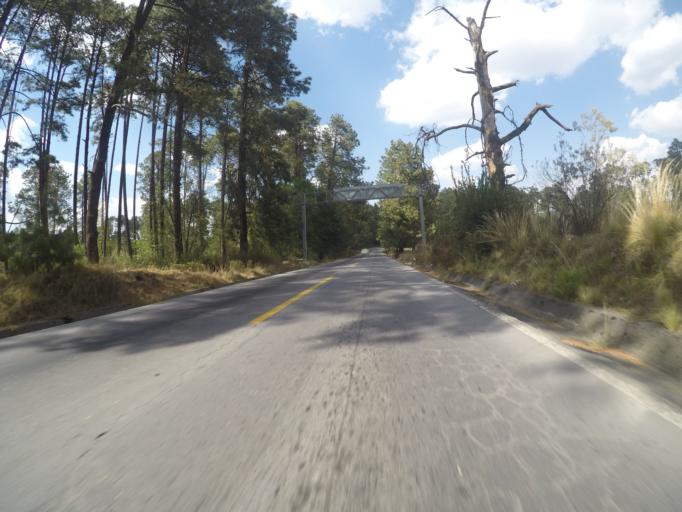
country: MX
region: Mexico
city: Cerro La Calera
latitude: 19.2072
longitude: -99.8093
